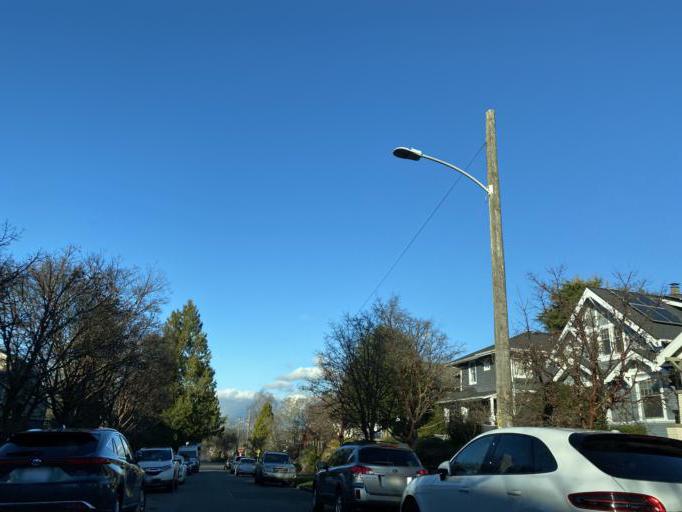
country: US
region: Washington
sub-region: King County
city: Seattle
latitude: 47.6402
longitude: -122.3583
